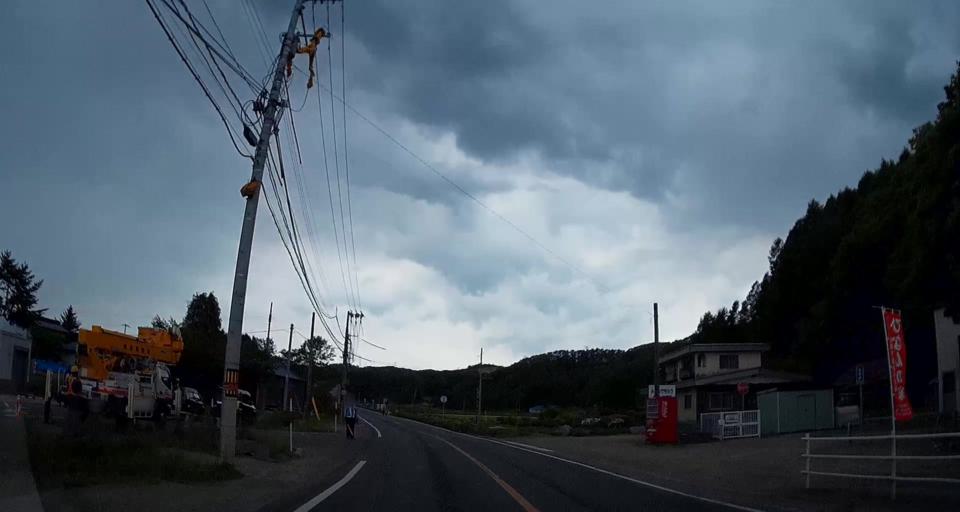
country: JP
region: Hokkaido
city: Chitose
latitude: 42.7583
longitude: 141.9257
